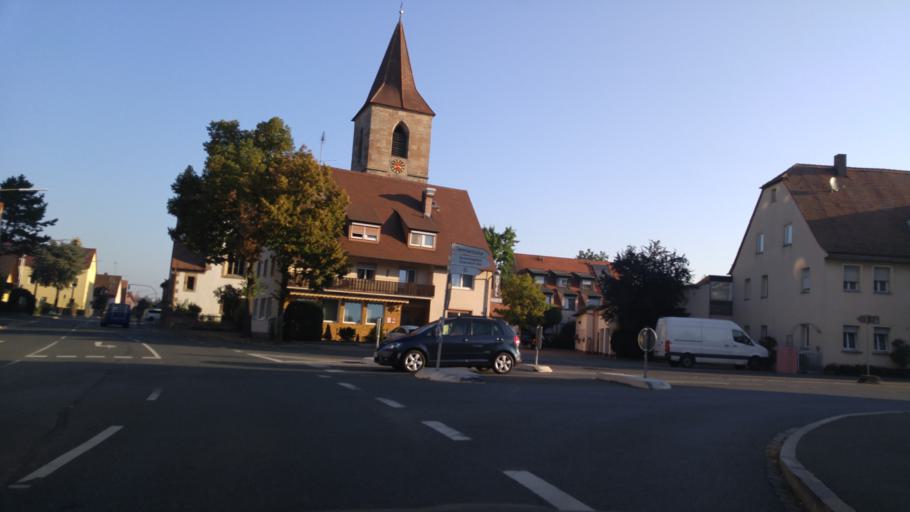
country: DE
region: Bavaria
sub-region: Regierungsbezirk Mittelfranken
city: Erlangen
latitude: 49.5529
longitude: 10.9890
